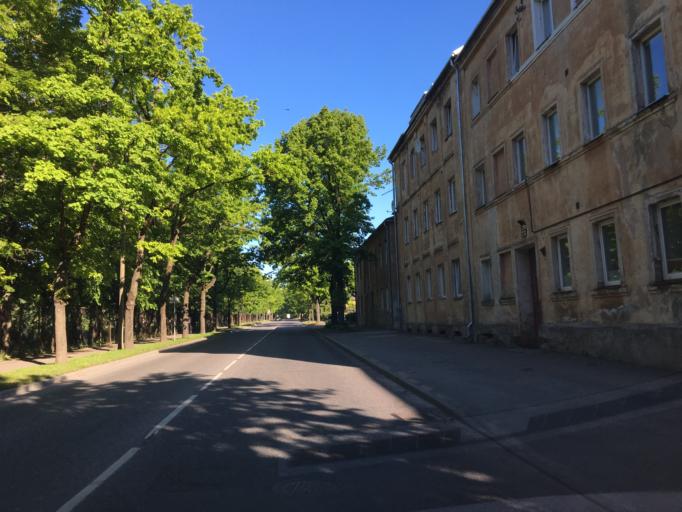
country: EE
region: Tartu
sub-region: Tartu linn
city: Tartu
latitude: 58.3902
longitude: 26.7271
